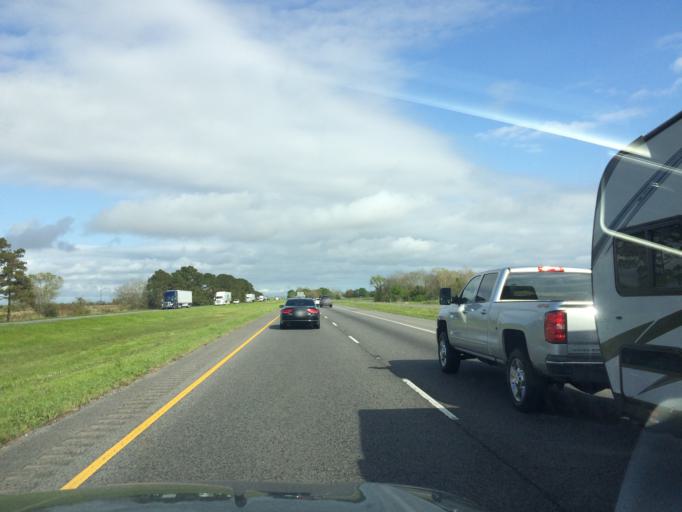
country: US
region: Louisiana
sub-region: Jefferson Davis Parish
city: Welsh
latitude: 30.2472
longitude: -92.7602
